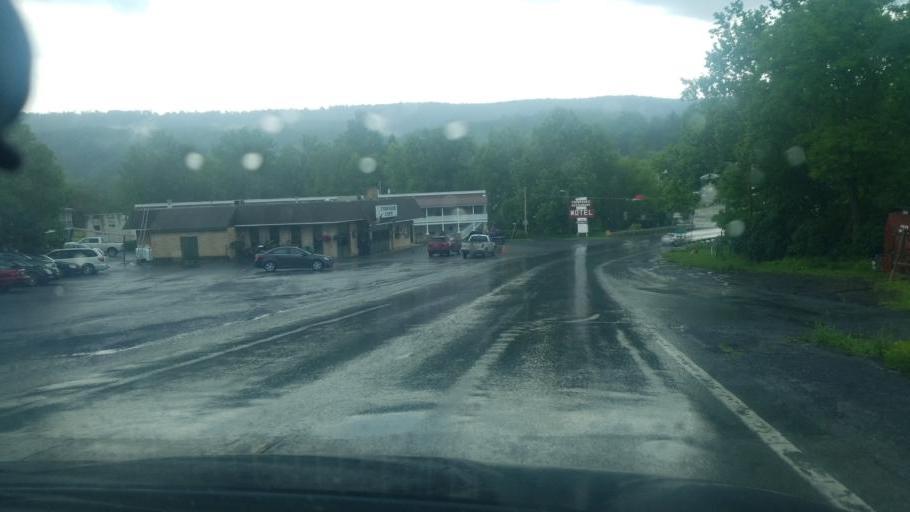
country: US
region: West Virginia
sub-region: Pendleton County
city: Franklin
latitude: 38.6540
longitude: -79.3319
